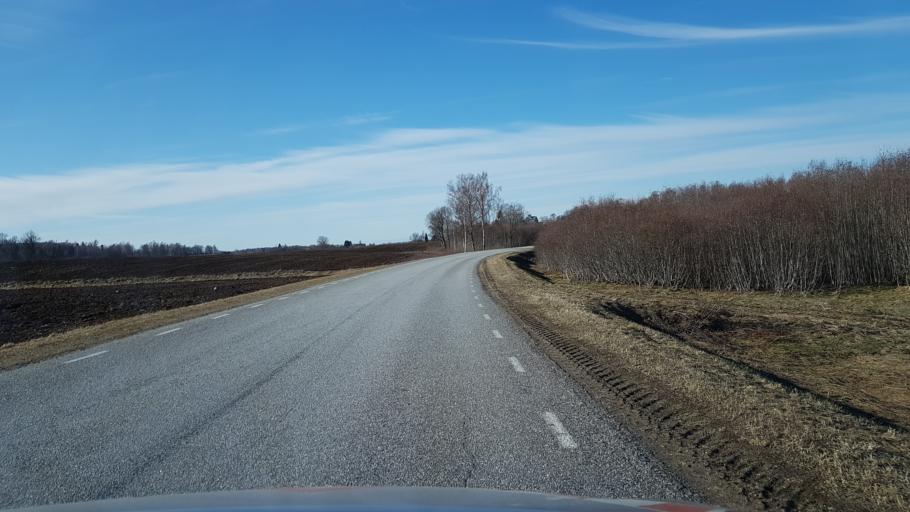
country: EE
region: Laeaene-Virumaa
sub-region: Kadrina vald
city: Kadrina
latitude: 59.3023
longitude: 26.1602
